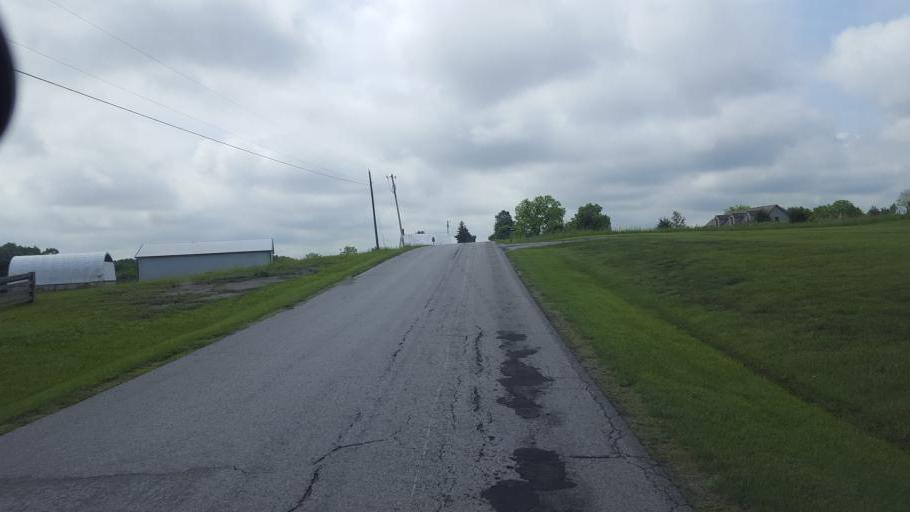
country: US
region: Ohio
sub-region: Delaware County
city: Ashley
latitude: 40.3934
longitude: -82.8756
